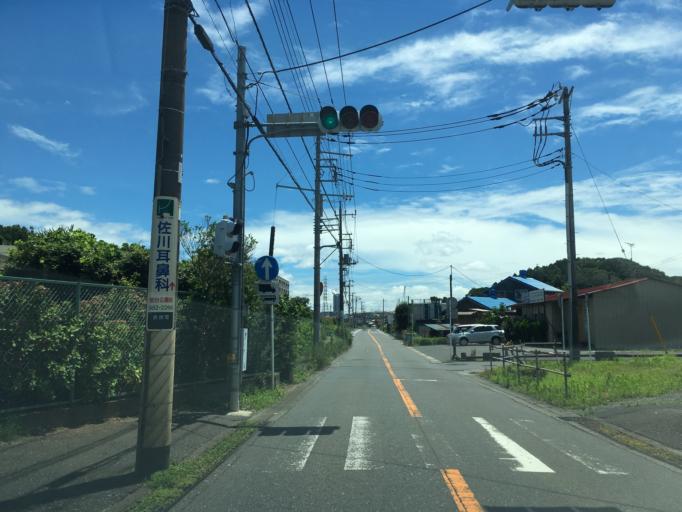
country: JP
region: Tokyo
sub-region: Machida-shi
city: Machida
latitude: 35.5516
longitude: 139.4903
